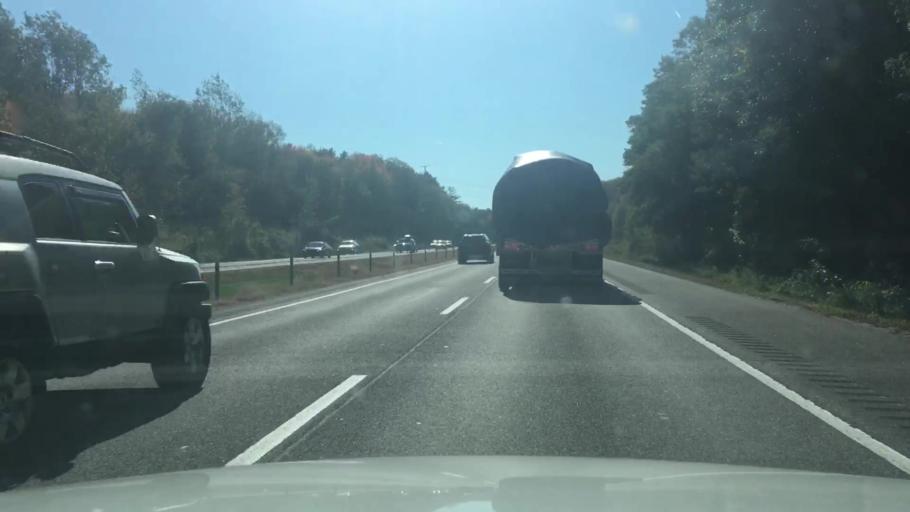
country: US
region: Maine
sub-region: Cumberland County
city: Yarmouth
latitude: 43.7912
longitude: -70.1834
